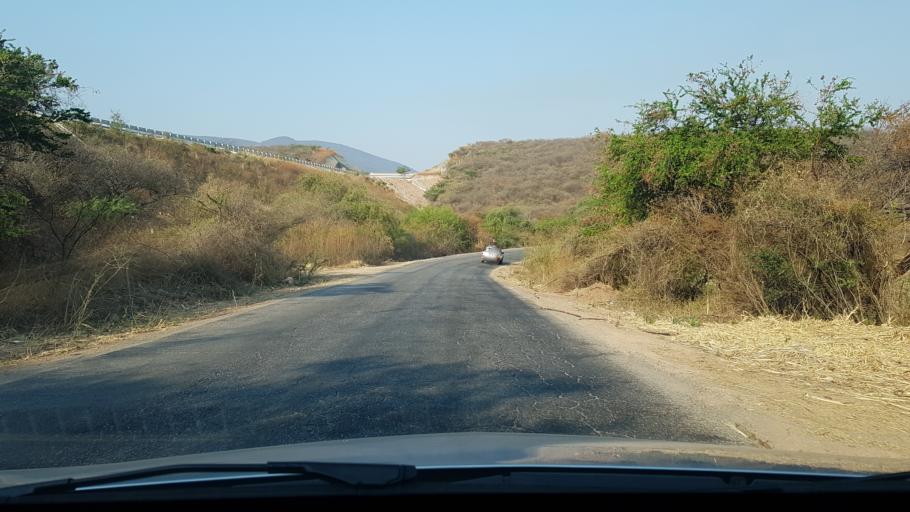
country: MX
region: Morelos
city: Tlaltizapan
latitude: 18.6780
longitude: -99.0851
